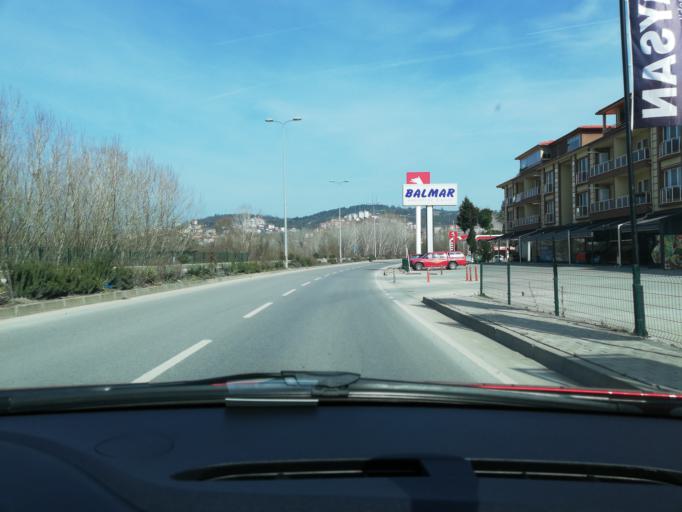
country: TR
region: Bartin
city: Bartin
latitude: 41.6334
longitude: 32.3486
